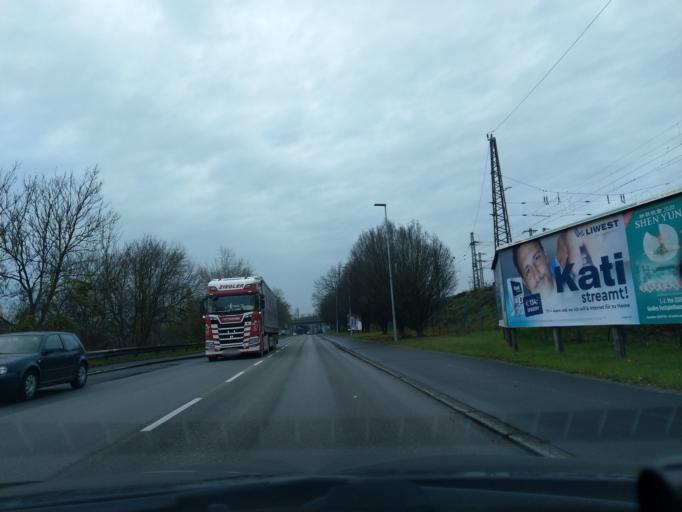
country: AT
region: Upper Austria
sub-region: Politischer Bezirk Urfahr-Umgebung
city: Steyregg
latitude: 48.2599
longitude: 14.3330
